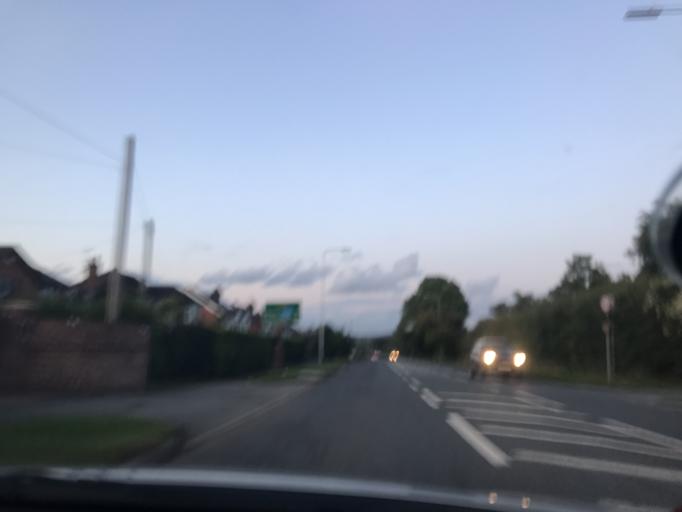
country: GB
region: England
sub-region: Cheshire West and Chester
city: Tarvin
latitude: 53.1973
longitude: -2.7688
